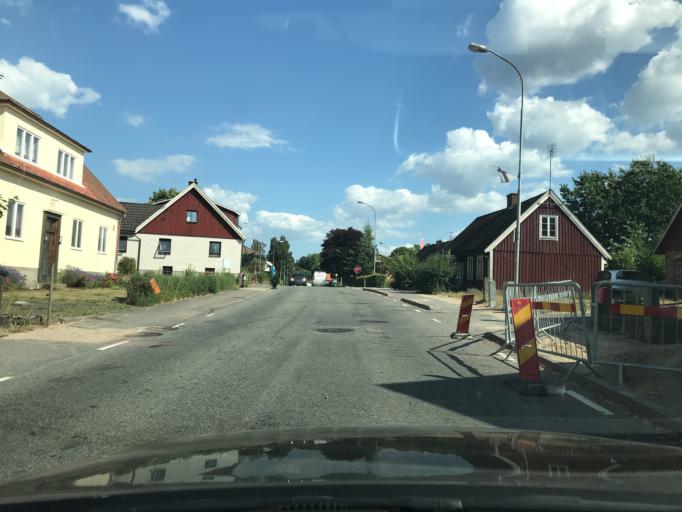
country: SE
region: Skane
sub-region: Hassleholms Kommun
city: Hastveda
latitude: 56.2848
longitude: 13.9341
